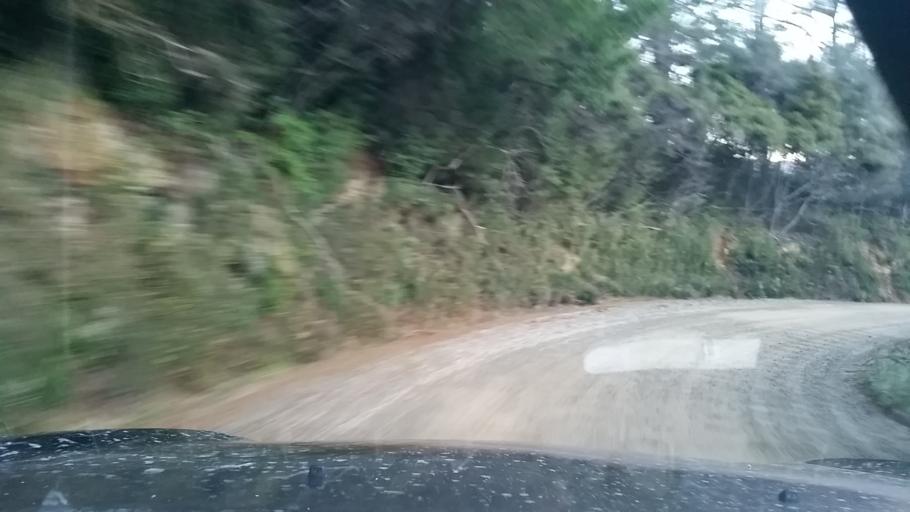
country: NZ
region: Marlborough
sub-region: Marlborough District
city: Picton
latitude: -41.1352
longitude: 174.1425
